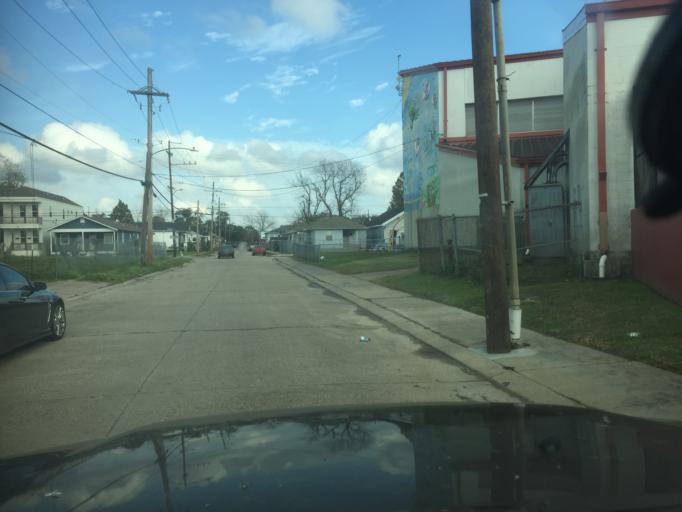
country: US
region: Louisiana
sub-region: Orleans Parish
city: New Orleans
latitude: 29.9929
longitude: -90.0753
